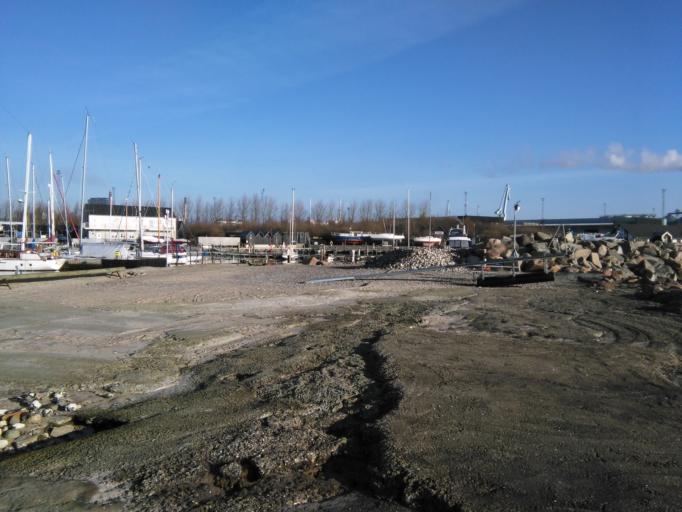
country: DK
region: Central Jutland
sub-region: Arhus Kommune
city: Arhus
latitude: 56.1382
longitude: 10.2182
